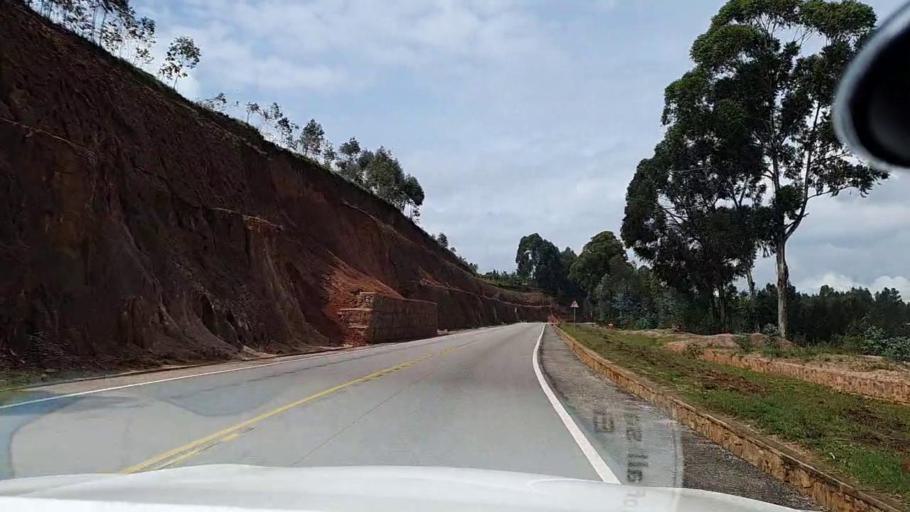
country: RW
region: Southern Province
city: Nzega
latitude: -2.4920
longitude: 29.5108
